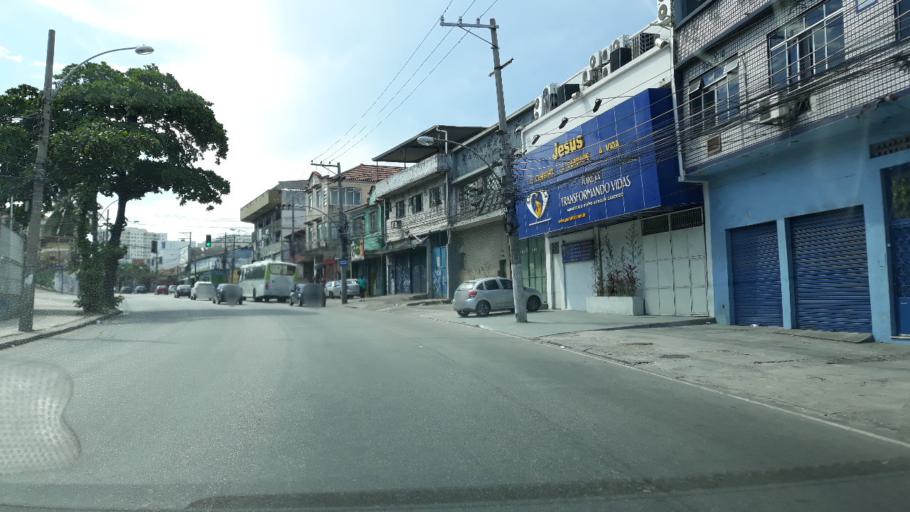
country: BR
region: Rio de Janeiro
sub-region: Rio De Janeiro
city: Rio de Janeiro
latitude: -22.8791
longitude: -43.2604
